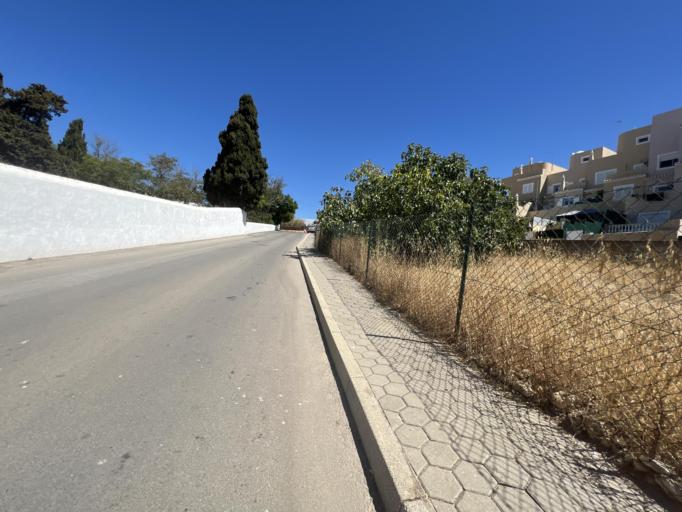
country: PT
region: Faro
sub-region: Portimao
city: Portimao
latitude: 37.1220
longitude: -8.5183
